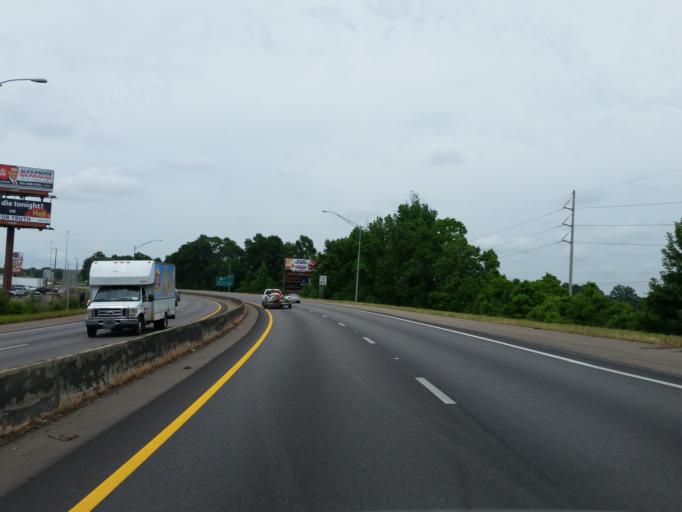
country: US
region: Mississippi
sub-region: Jones County
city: Laurel
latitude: 31.6909
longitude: -89.1178
